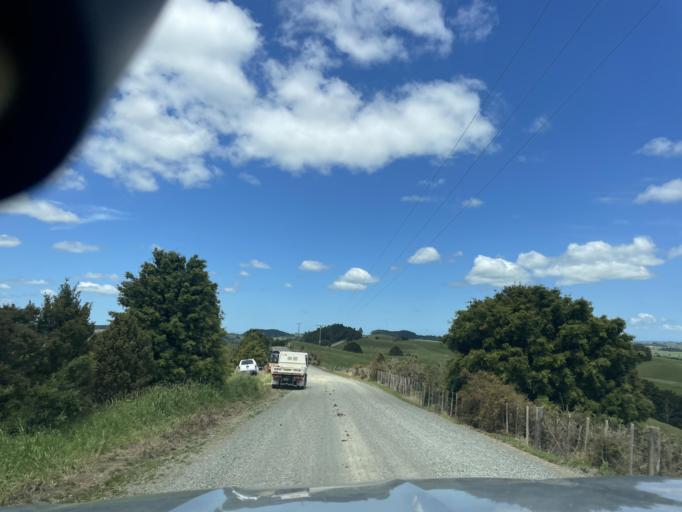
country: NZ
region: Auckland
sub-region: Auckland
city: Wellsford
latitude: -36.1576
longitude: 174.5393
